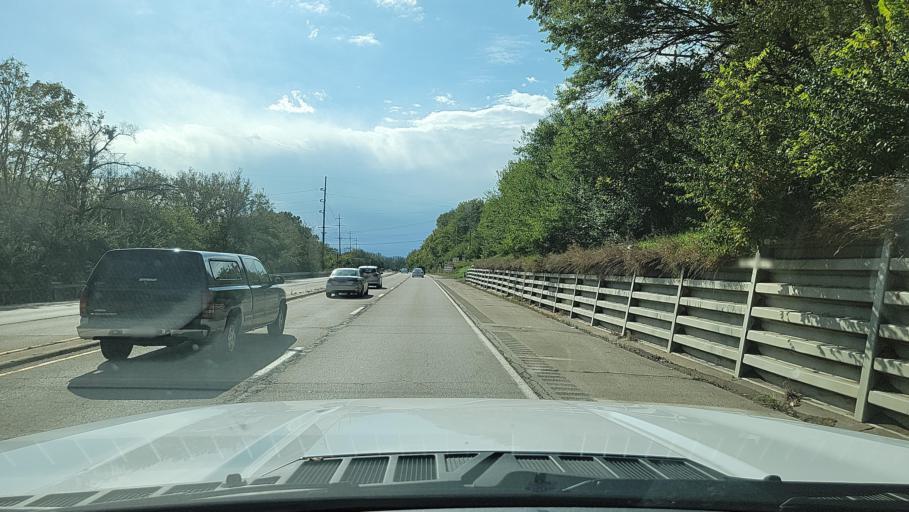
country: US
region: Illinois
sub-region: Tazewell County
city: Pekin
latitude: 40.5876
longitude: -89.6810
